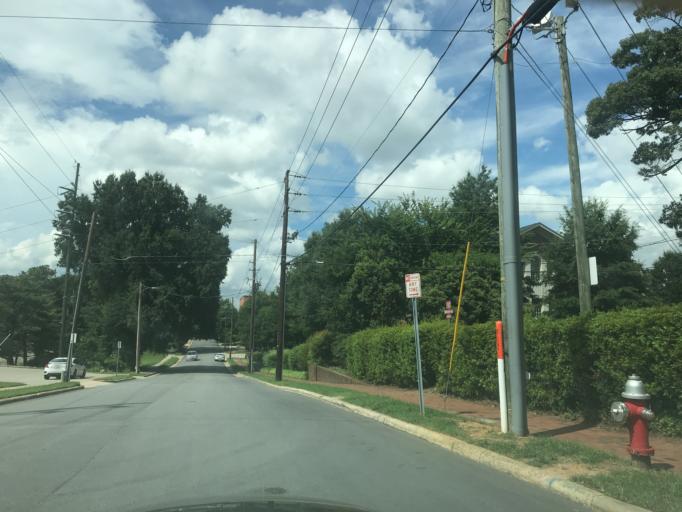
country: US
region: North Carolina
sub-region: Wake County
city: Raleigh
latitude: 35.7899
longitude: -78.6385
